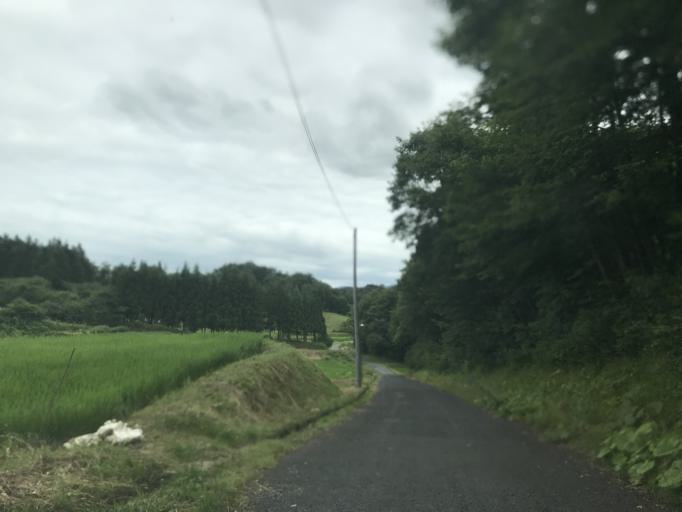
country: JP
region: Iwate
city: Ichinoseki
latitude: 38.9062
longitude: 141.0707
